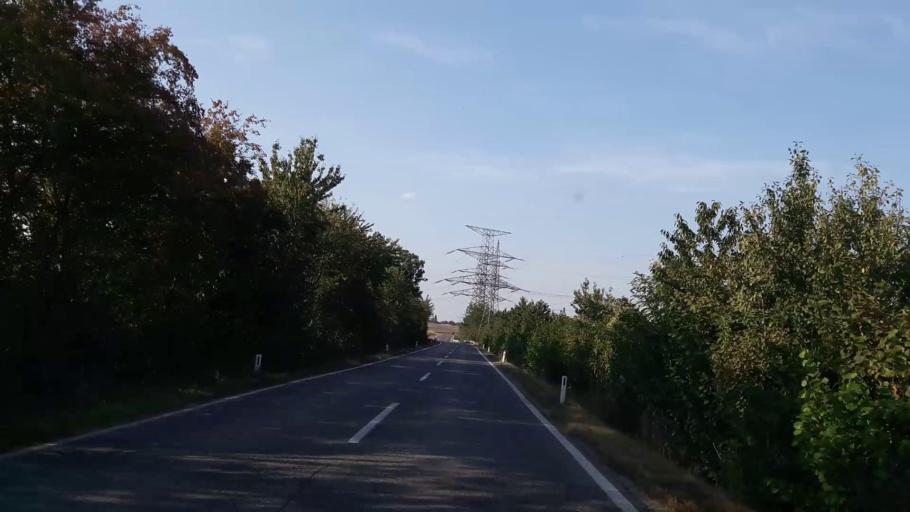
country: AT
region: Lower Austria
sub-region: Politischer Bezirk Ganserndorf
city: Mannsdorf an der Donau
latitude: 48.0937
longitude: 16.6680
